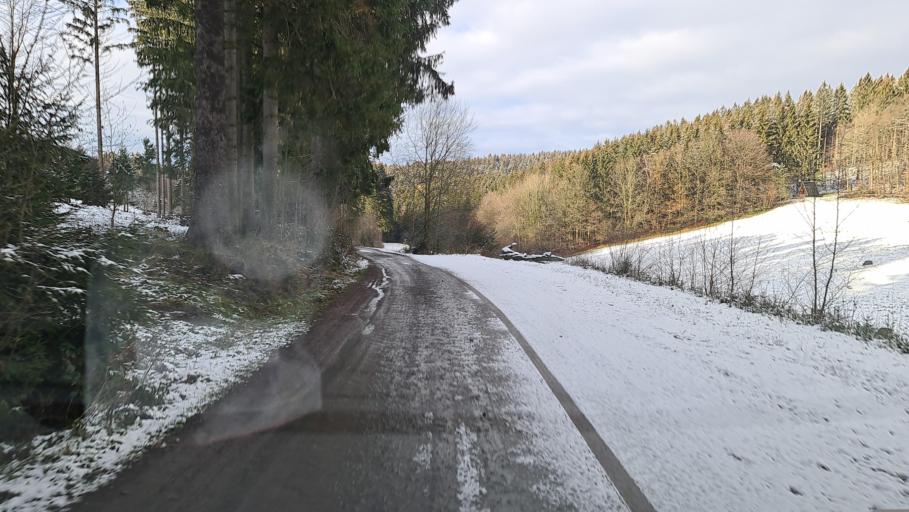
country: DE
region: Saxony
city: Dorfchemnitz
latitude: 50.7802
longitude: 13.4346
